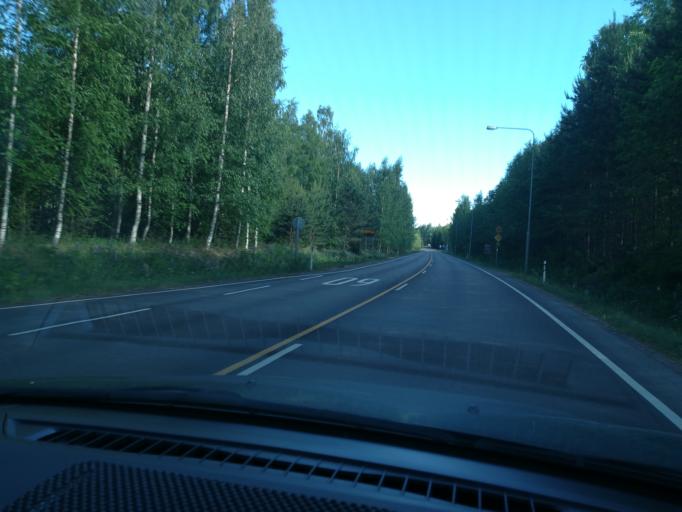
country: FI
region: Southern Savonia
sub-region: Mikkeli
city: Puumala
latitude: 61.5150
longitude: 28.1742
